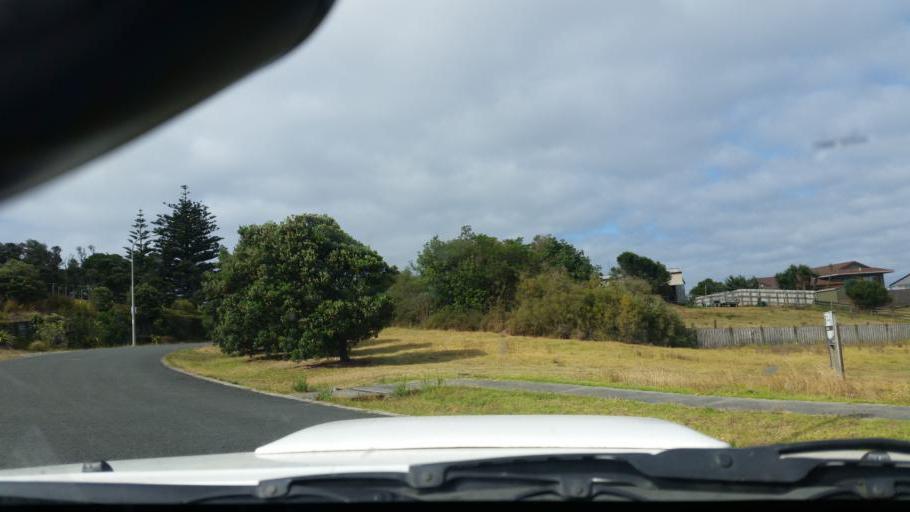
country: NZ
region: Northland
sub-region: Kaipara District
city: Dargaville
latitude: -35.9490
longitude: 173.7486
